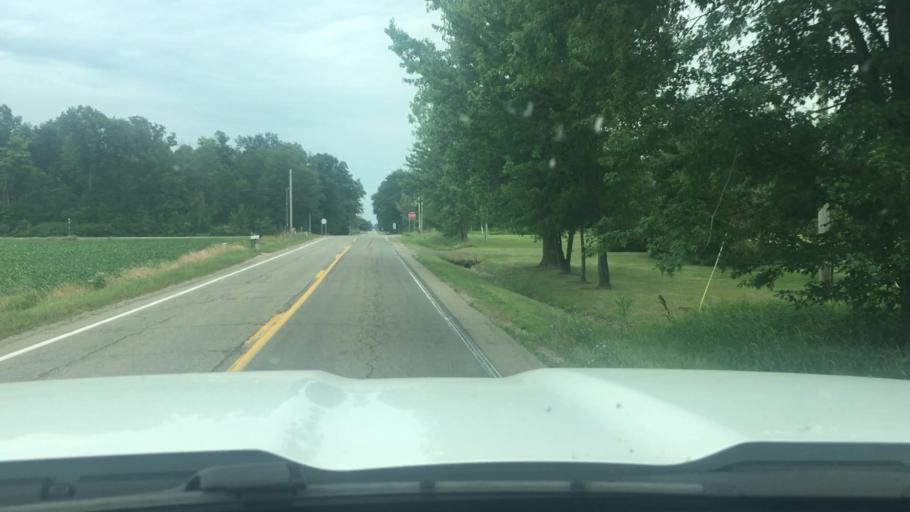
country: US
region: Michigan
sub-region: Clinton County
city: Saint Johns
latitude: 43.0021
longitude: -84.4840
